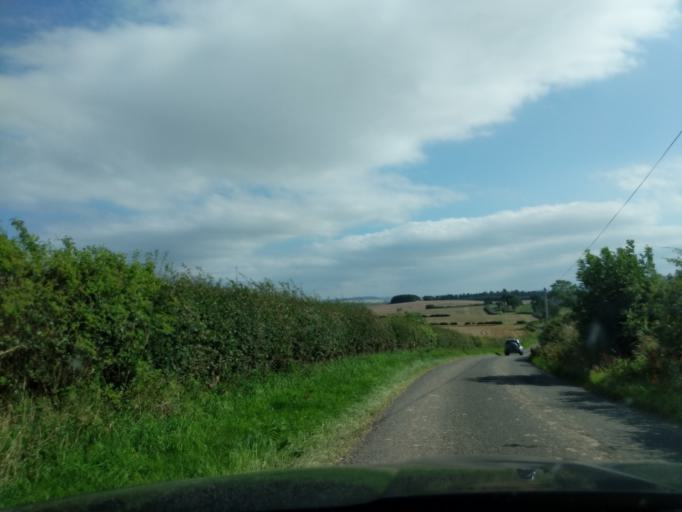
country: GB
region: England
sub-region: Northumberland
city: Ford
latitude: 55.6536
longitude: -2.1467
